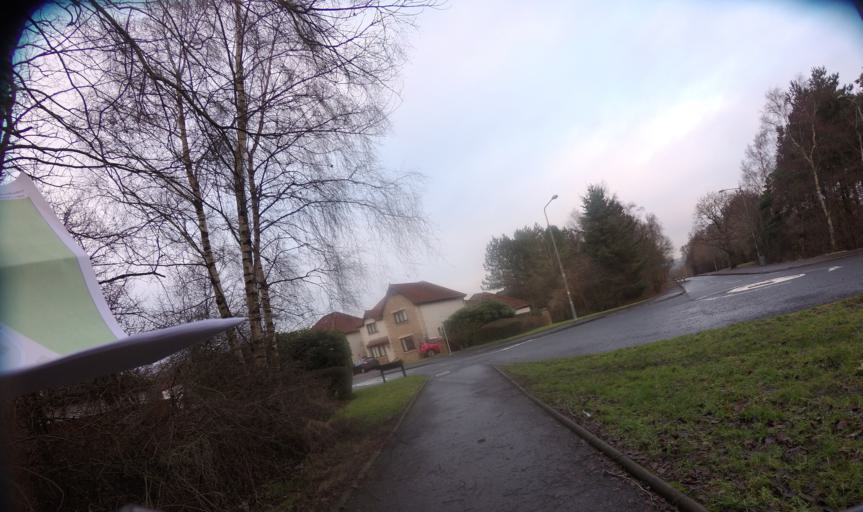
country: GB
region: Scotland
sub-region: West Lothian
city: Livingston
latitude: 55.8719
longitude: -3.5316
